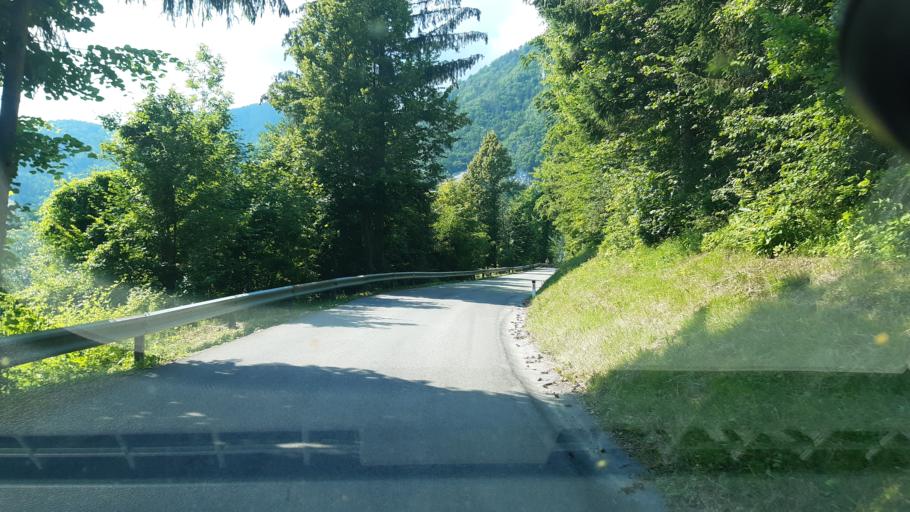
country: SI
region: Radovljica
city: Radovljica
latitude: 46.3766
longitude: 14.2154
